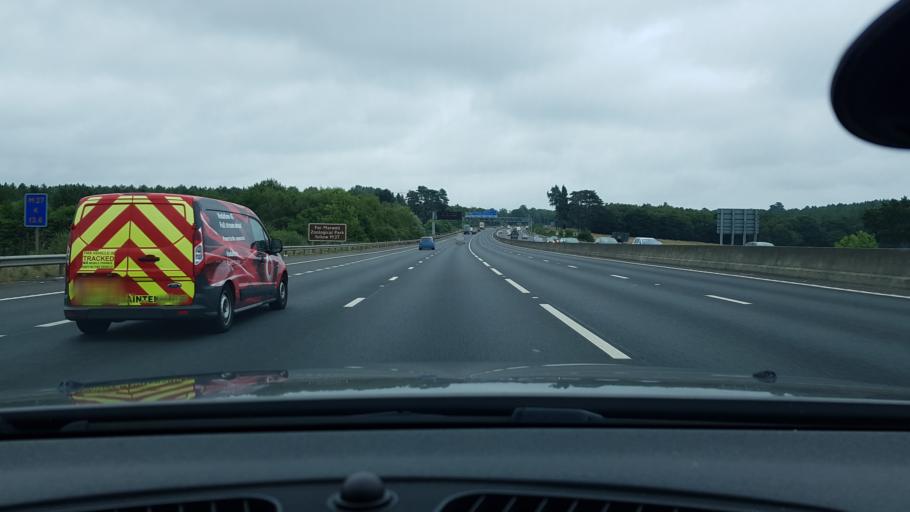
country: GB
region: England
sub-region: Hampshire
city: Totton
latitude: 50.9590
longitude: -1.4422
